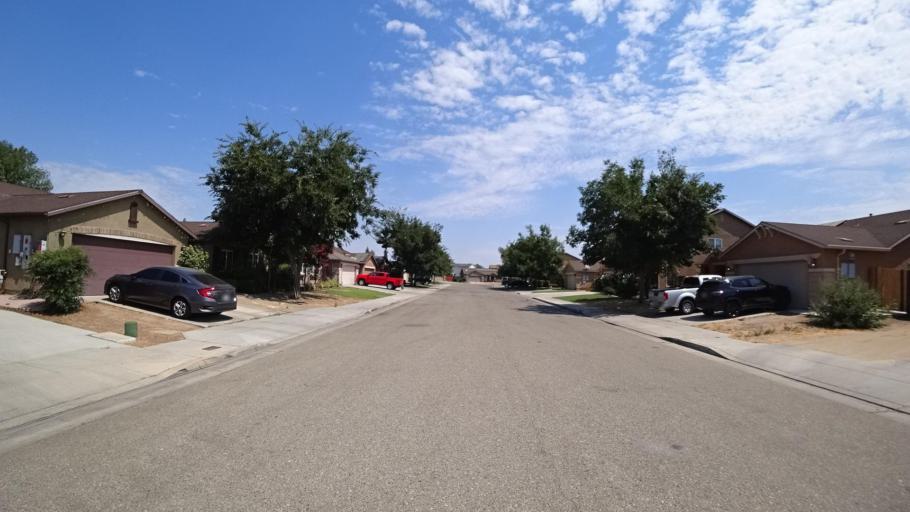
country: US
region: California
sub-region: Fresno County
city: Sunnyside
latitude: 36.7381
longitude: -119.6916
